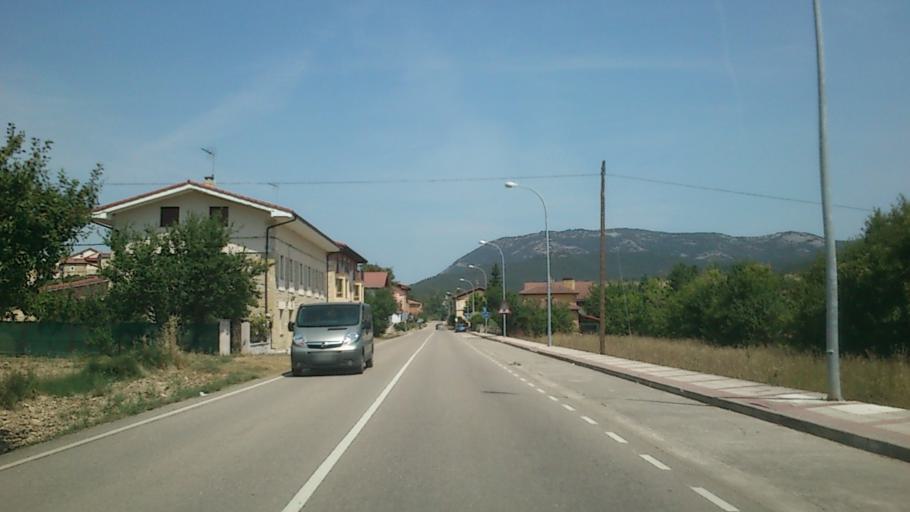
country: ES
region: Castille and Leon
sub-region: Provincia de Burgos
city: Trespaderne
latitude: 42.8497
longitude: -3.3346
